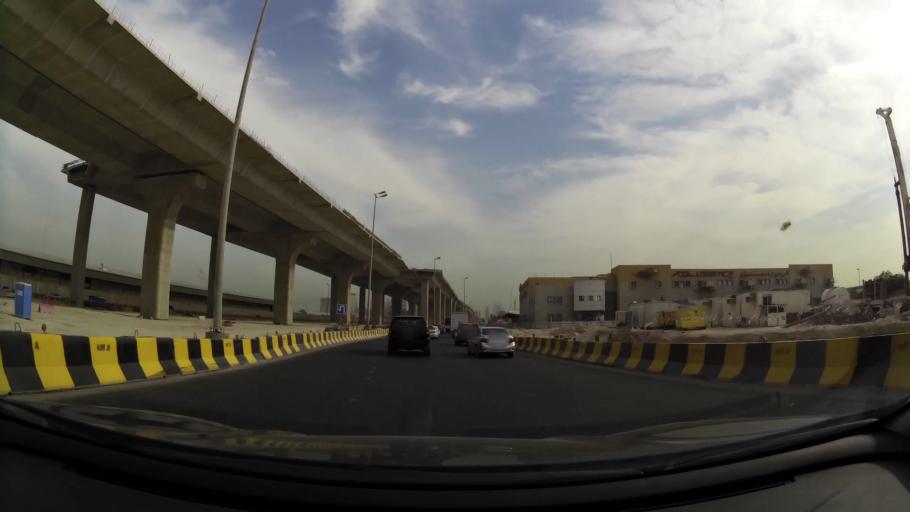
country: KW
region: Al Asimah
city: Ash Shamiyah
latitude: 29.3406
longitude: 47.9273
